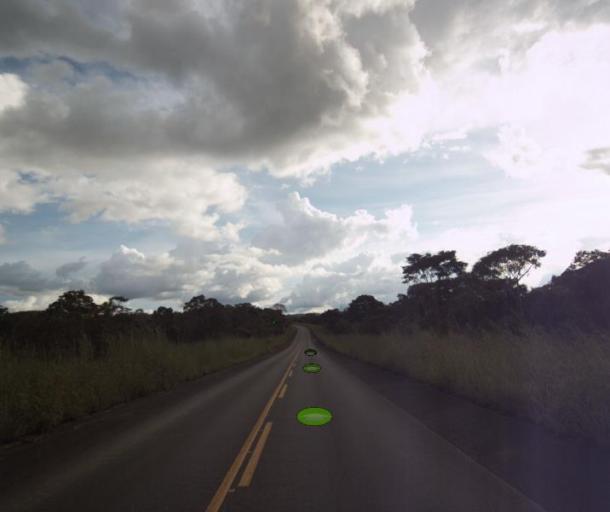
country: BR
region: Goias
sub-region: Niquelandia
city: Niquelandia
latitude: -14.5304
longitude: -48.5321
